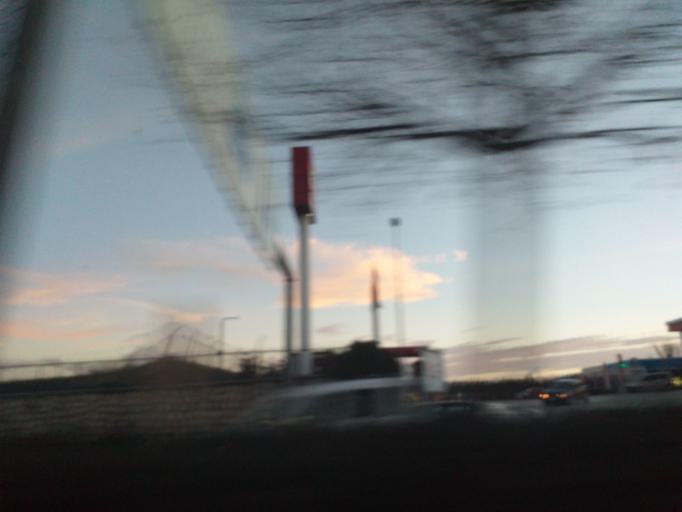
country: TR
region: Ankara
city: Batikent
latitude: 39.9453
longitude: 32.7314
